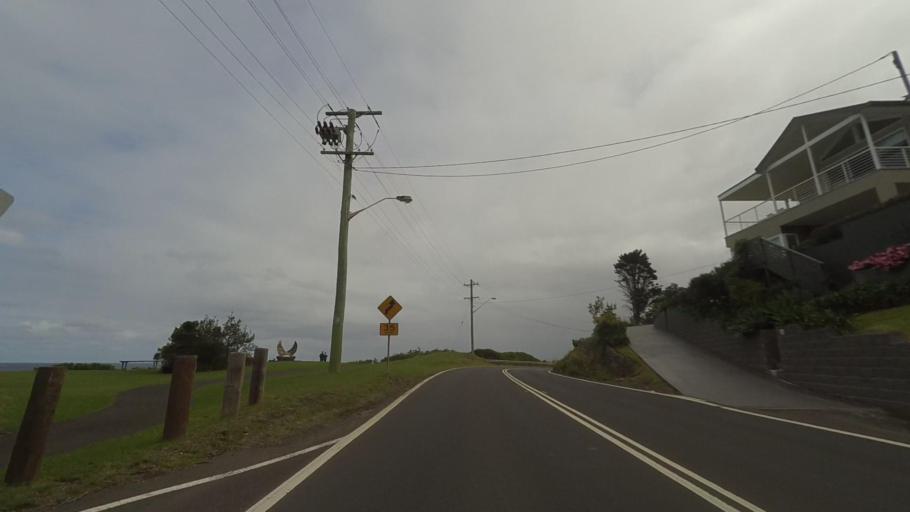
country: AU
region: New South Wales
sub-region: Wollongong
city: Bulli
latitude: -34.2849
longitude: 150.9505
